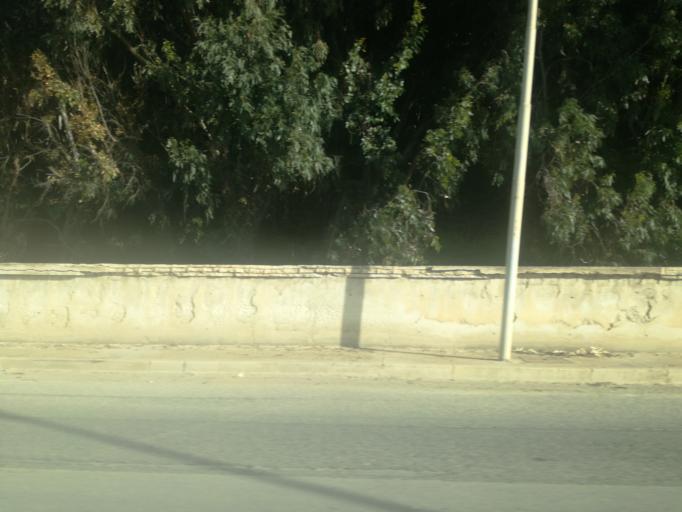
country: IT
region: Sicily
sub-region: Provincia di Caltanissetta
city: Gela
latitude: 37.0686
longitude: 14.2267
